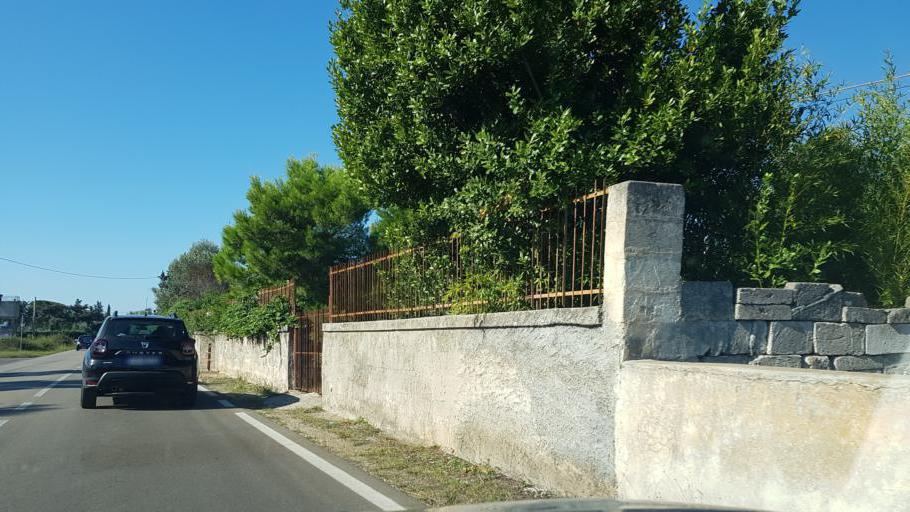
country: IT
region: Apulia
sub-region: Provincia di Lecce
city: Monteroni di Lecce
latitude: 40.3236
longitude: 18.0759
